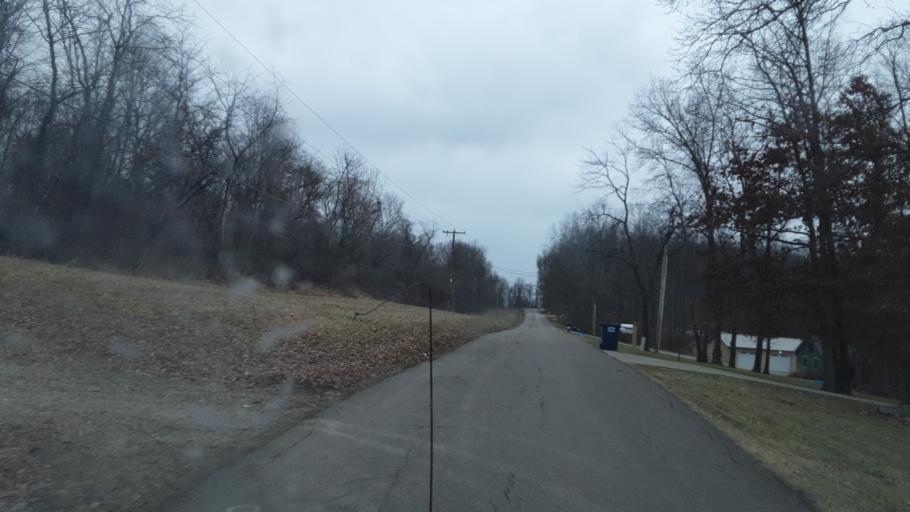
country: US
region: Ohio
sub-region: Perry County
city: Thornport
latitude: 39.9394
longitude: -82.3709
